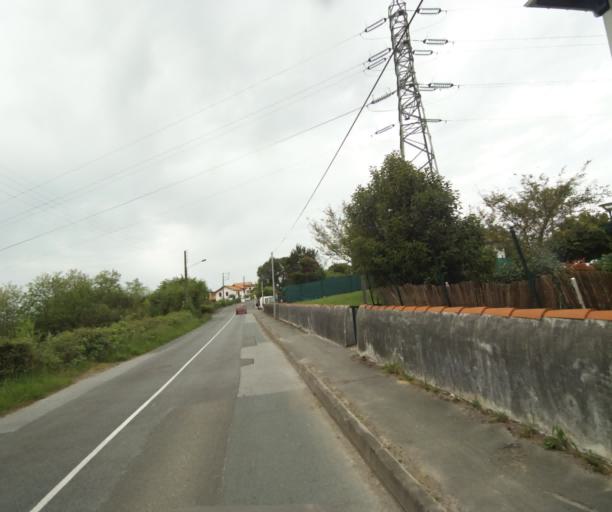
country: FR
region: Aquitaine
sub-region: Departement des Pyrenees-Atlantiques
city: Mouguerre
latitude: 43.4650
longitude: -1.4431
